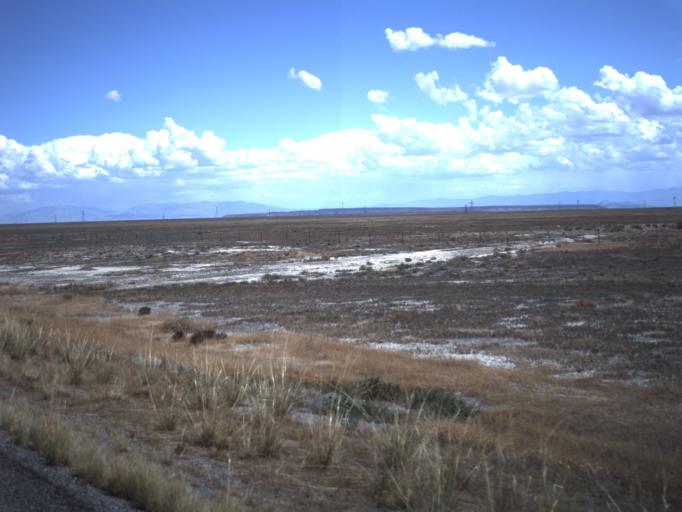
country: US
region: Utah
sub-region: Millard County
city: Delta
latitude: 39.2241
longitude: -112.9425
